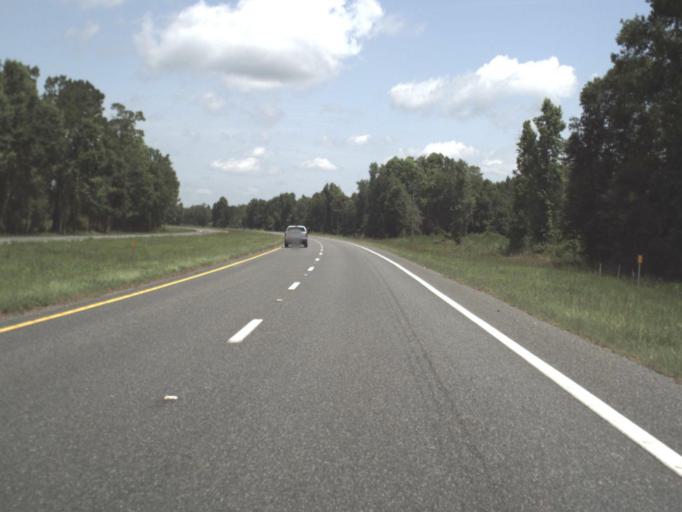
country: US
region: Florida
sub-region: Taylor County
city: Perry
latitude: 29.9436
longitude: -83.4502
